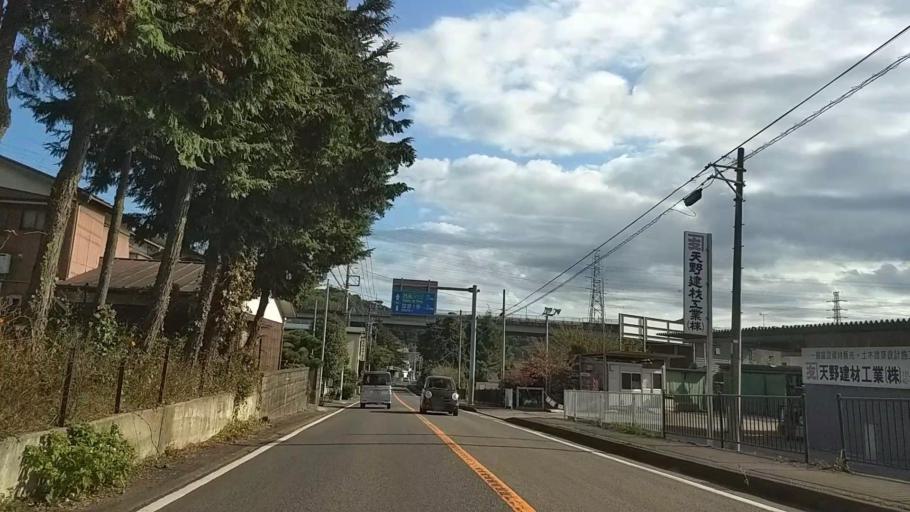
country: JP
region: Kanagawa
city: Ninomiya
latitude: 35.2920
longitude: 139.2016
